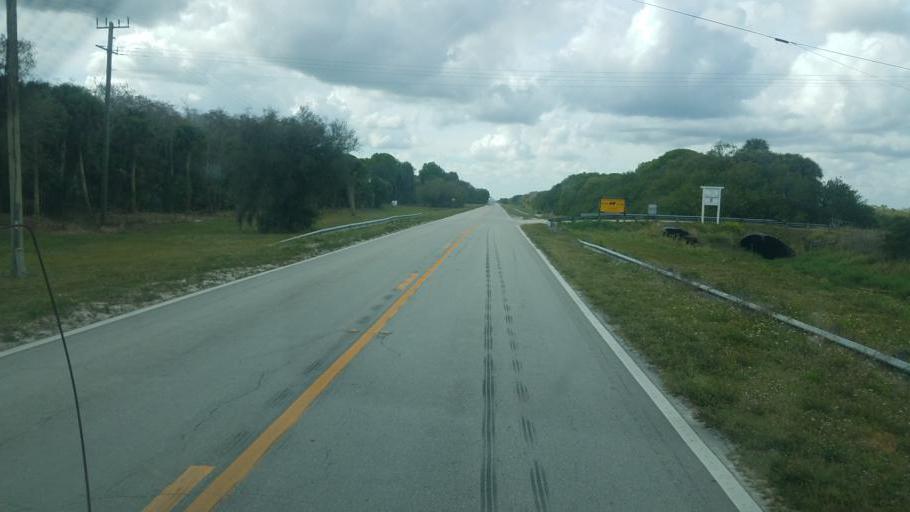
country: US
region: Florida
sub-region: Indian River County
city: West Vero Corridor
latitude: 27.4484
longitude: -80.6284
